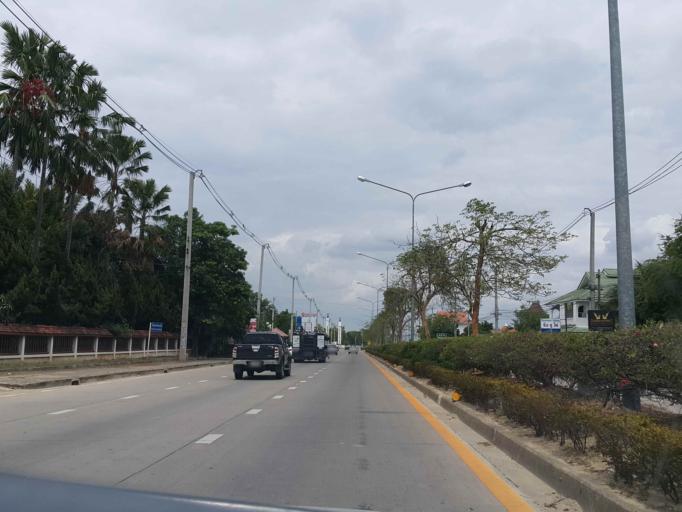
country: TH
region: Chiang Mai
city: Chiang Mai
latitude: 18.7488
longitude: 98.9446
